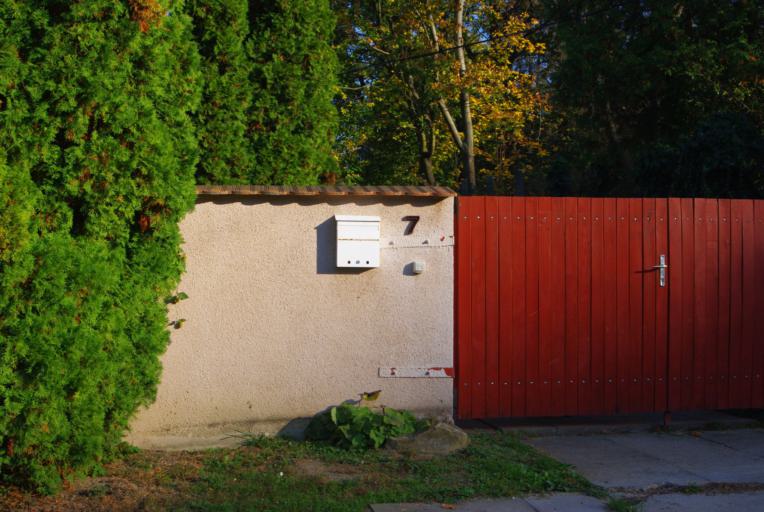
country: HU
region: Pest
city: Nagymaros
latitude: 47.7601
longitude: 18.9216
